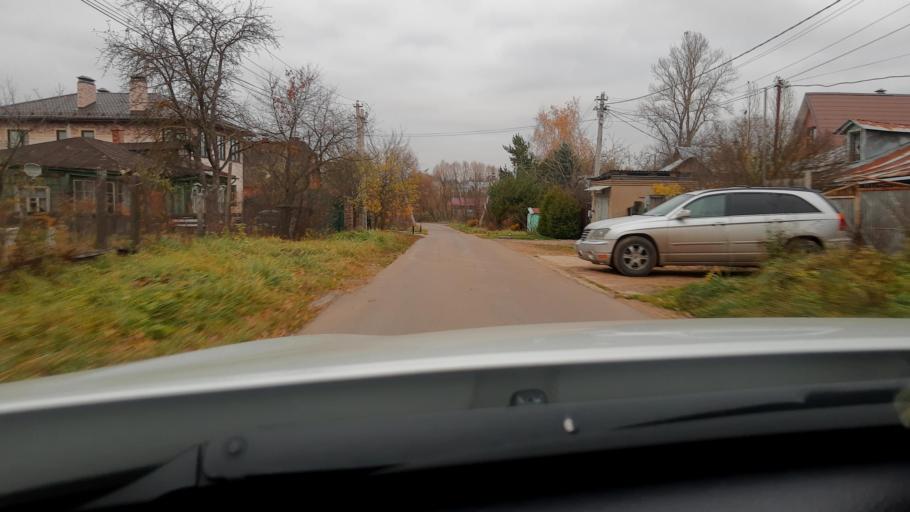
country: RU
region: Moscow
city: Vnukovo
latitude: 55.6022
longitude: 37.2309
